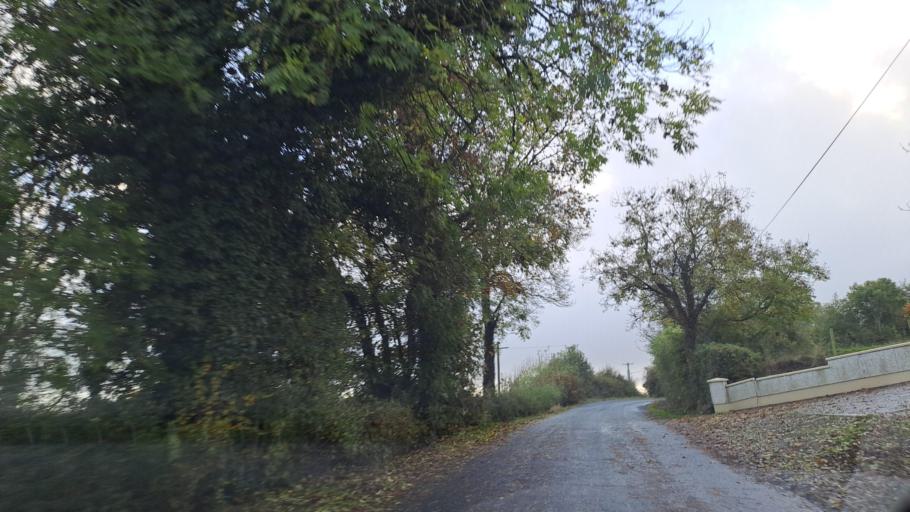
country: IE
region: Ulster
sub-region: County Monaghan
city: Carrickmacross
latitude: 53.9704
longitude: -6.7751
